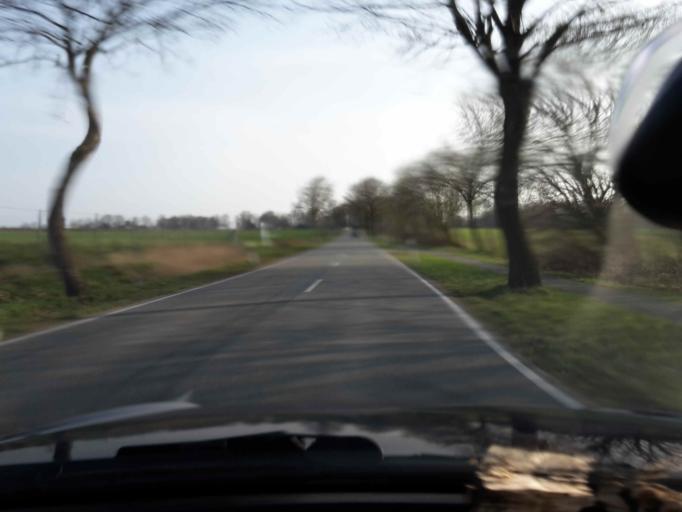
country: DE
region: Lower Saxony
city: Buxtehude
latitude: 53.4439
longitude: 9.6930
